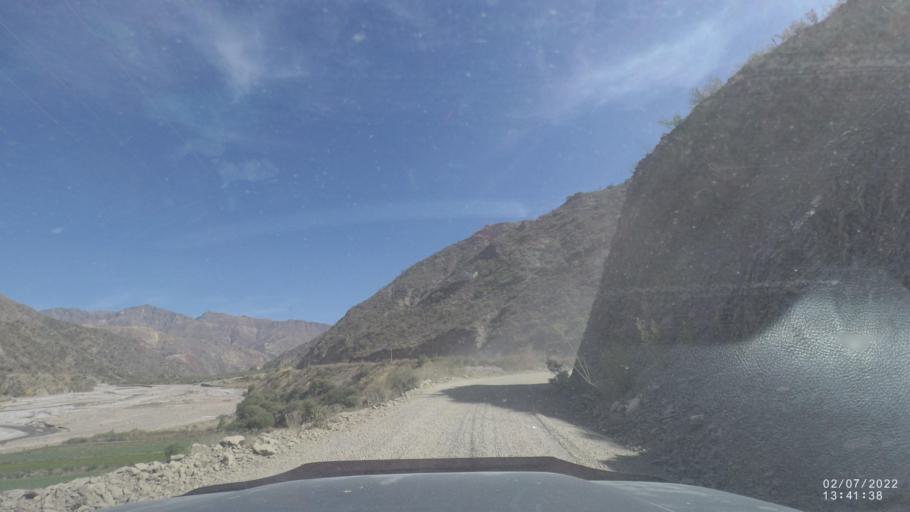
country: BO
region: Cochabamba
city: Irpa Irpa
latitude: -17.7982
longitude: -66.3528
